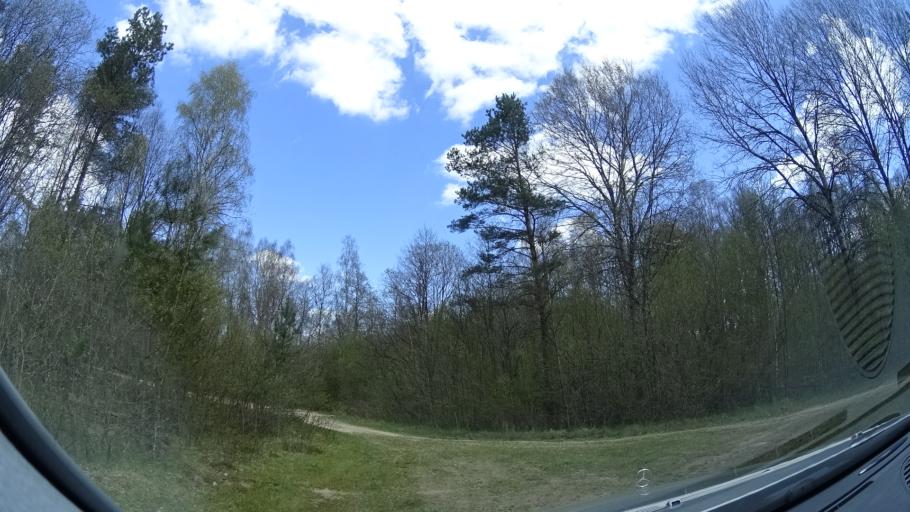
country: SE
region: Skane
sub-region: Hassleholms Kommun
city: Tormestorp
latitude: 56.0958
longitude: 13.7156
